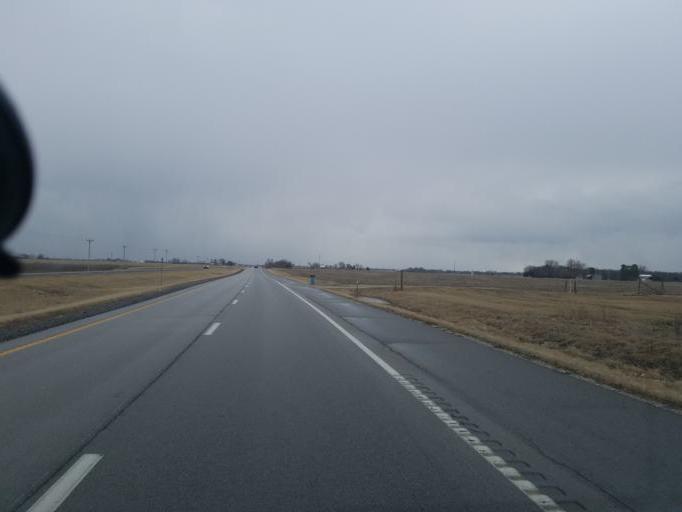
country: US
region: Missouri
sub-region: Macon County
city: Macon
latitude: 39.8421
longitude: -92.4807
